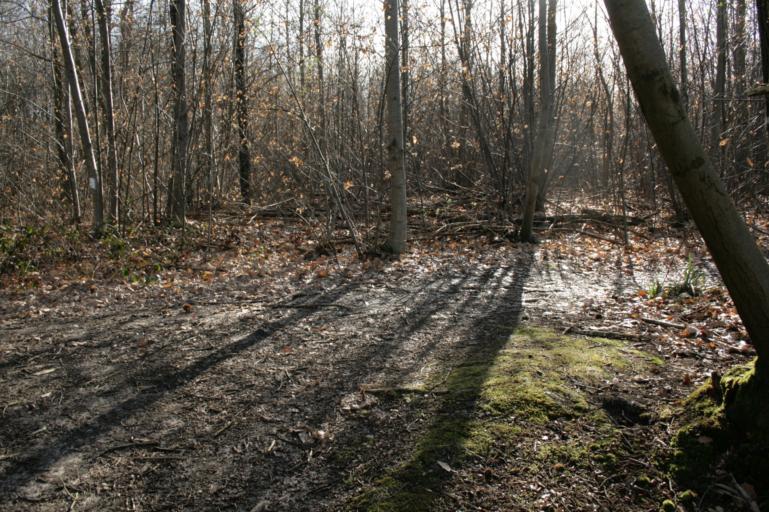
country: FR
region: Ile-de-France
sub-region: Departement des Yvelines
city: Vaux-sur-Seine
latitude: 49.0132
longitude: 1.9846
